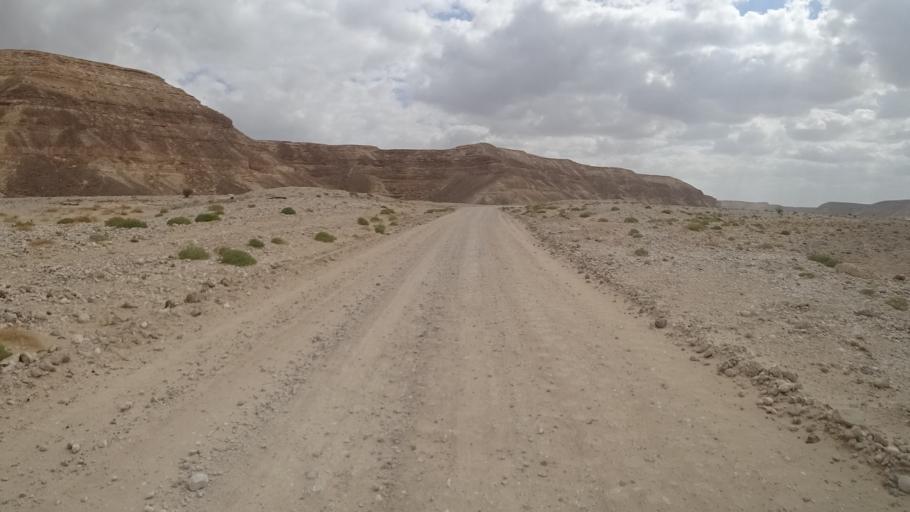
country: YE
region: Al Mahrah
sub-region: Shahan
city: Shihan as Sufla
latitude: 17.4620
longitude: 53.0077
